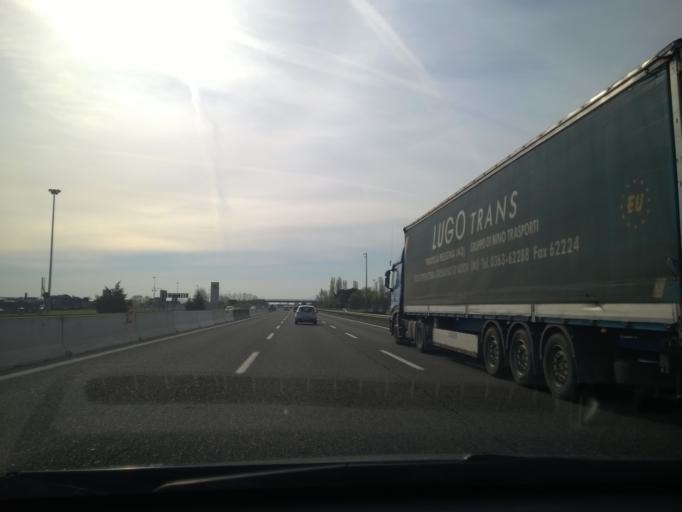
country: IT
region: Emilia-Romagna
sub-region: Forli-Cesena
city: Santa Maria Nuova
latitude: 44.2172
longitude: 12.1768
